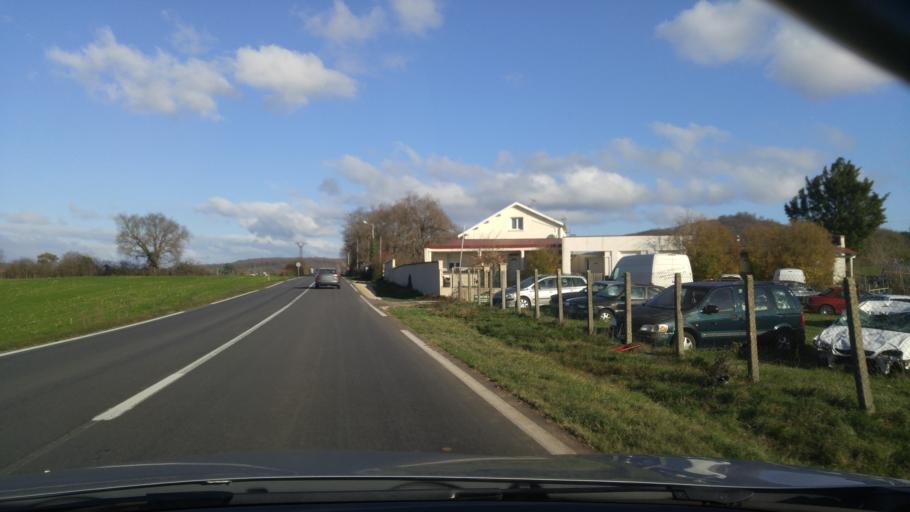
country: FR
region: Rhone-Alpes
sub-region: Departement de l'Isere
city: Chamagnieu
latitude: 45.6744
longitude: 5.1576
